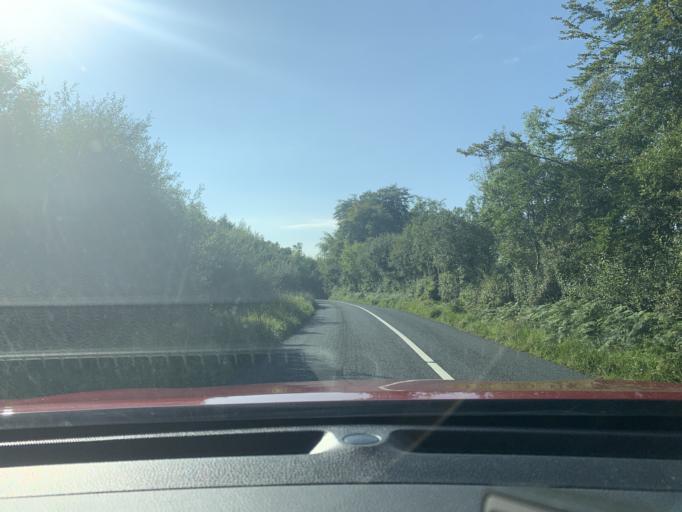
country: IE
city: Ballisodare
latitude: 54.1942
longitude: -8.5815
